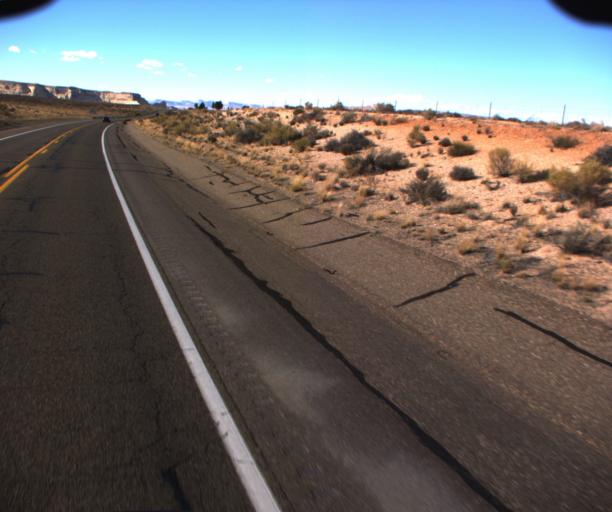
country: US
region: Arizona
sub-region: Coconino County
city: Page
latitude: 36.9855
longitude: -111.5547
